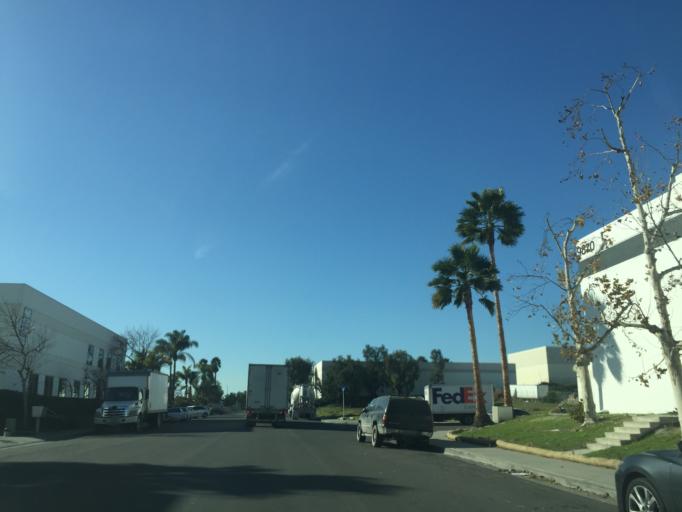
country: MX
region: Baja California
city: Tijuana
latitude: 32.5544
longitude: -116.9336
